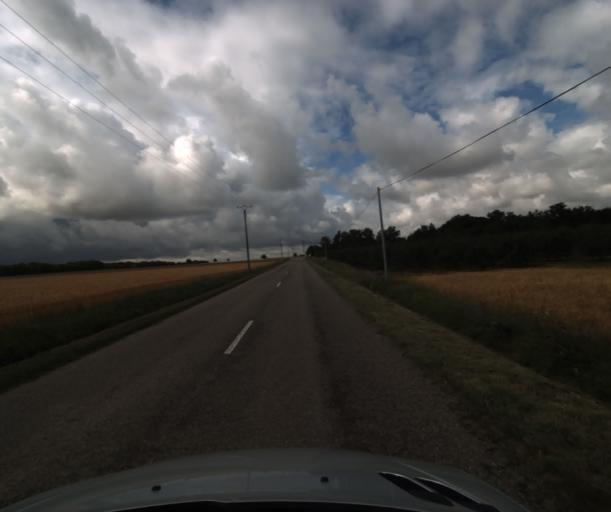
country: FR
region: Midi-Pyrenees
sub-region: Departement du Tarn-et-Garonne
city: Lavit
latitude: 43.9880
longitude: 0.9775
